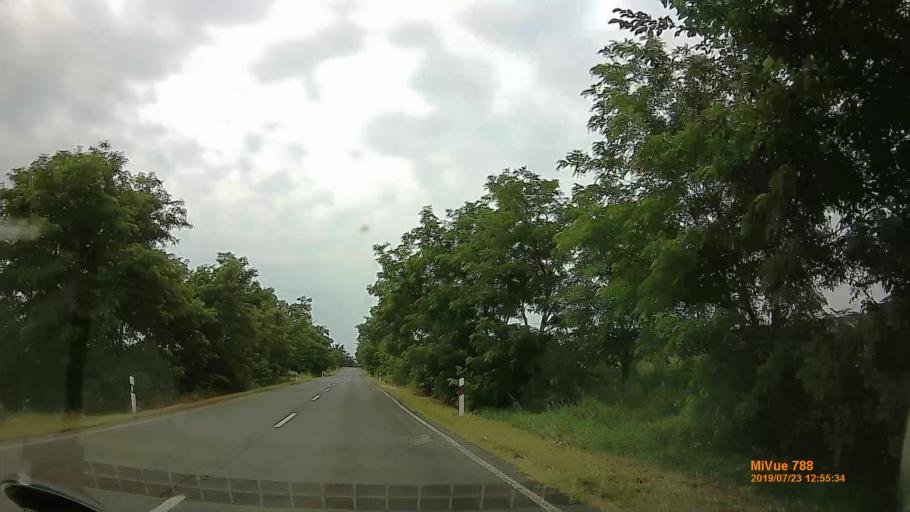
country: HU
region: Szabolcs-Szatmar-Bereg
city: Nagycserkesz
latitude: 47.9592
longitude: 21.5164
